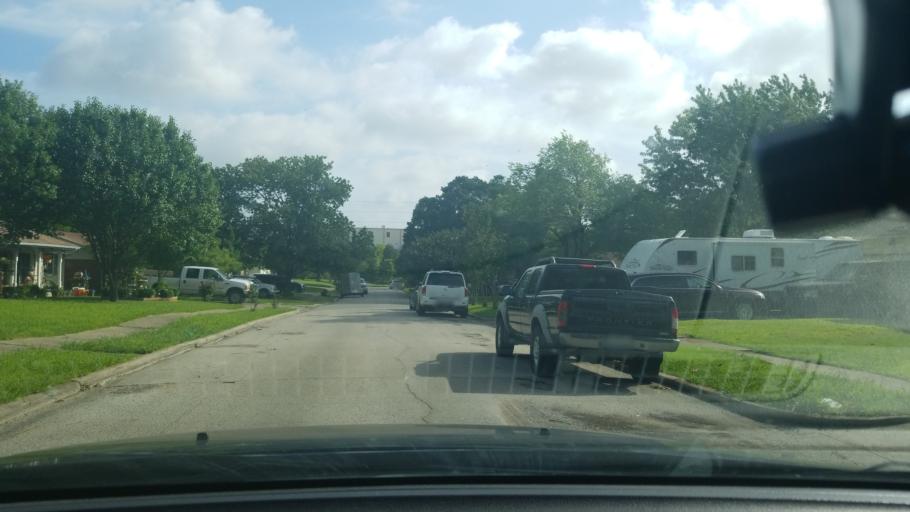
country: US
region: Texas
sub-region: Dallas County
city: Mesquite
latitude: 32.7721
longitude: -96.6314
